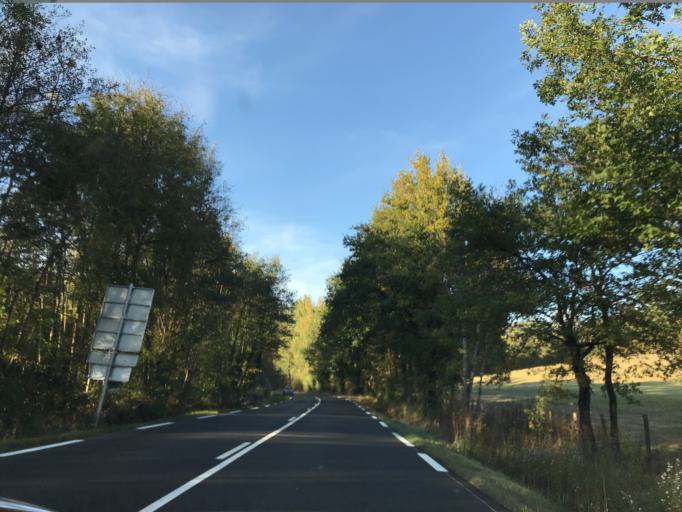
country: FR
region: Auvergne
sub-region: Departement du Puy-de-Dome
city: Paslieres
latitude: 45.8853
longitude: 3.5228
